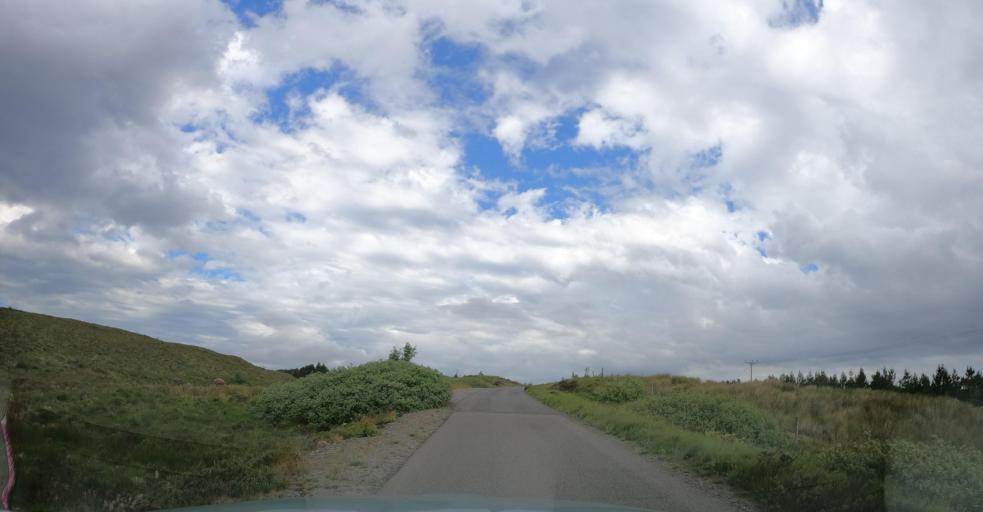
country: GB
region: Scotland
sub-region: Eilean Siar
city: Stornoway
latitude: 58.2016
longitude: -6.4092
